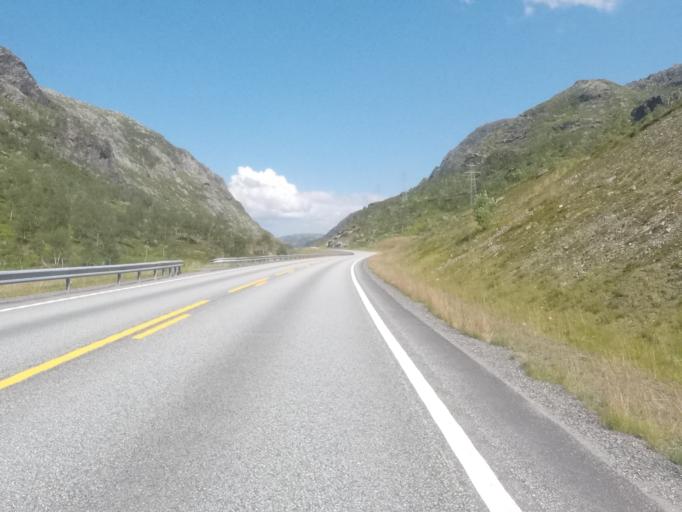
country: NO
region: Hordaland
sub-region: Modalen
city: Mo
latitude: 60.8041
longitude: 5.6172
